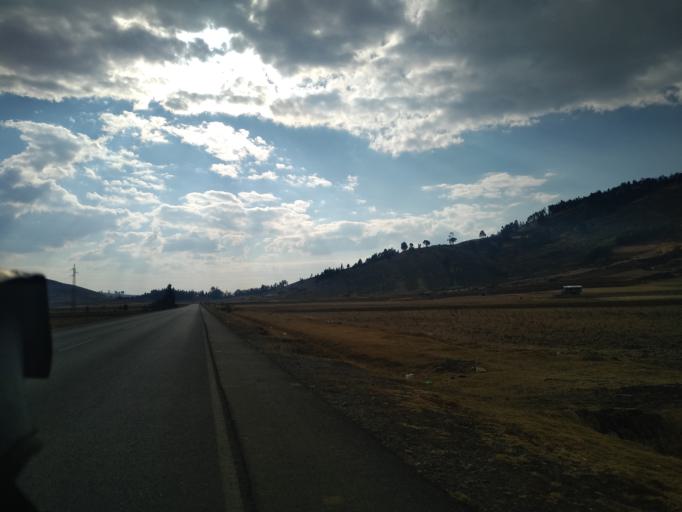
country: PE
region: Cajamarca
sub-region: Provincia de Cajamarca
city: Encanada
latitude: -7.1390
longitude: -78.3816
